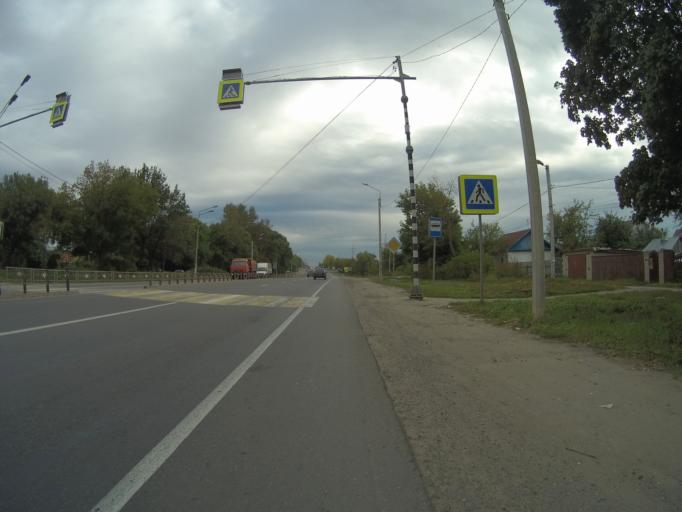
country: RU
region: Vladimir
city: Vladimir
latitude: 56.1424
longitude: 40.3562
